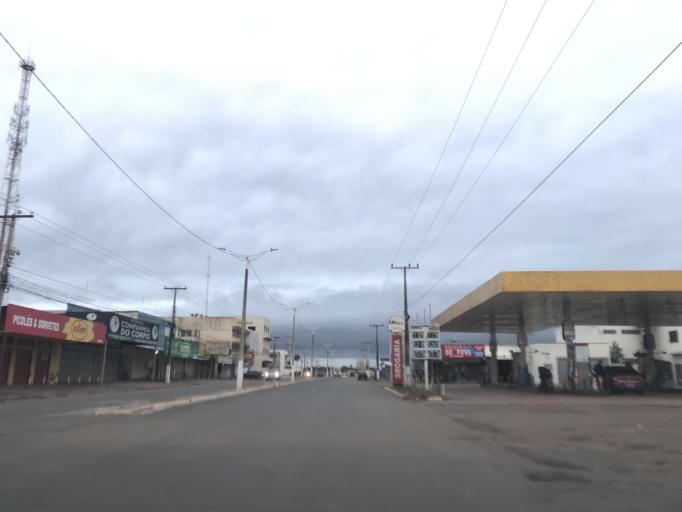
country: BR
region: Goias
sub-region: Luziania
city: Luziania
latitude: -16.2367
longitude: -47.9419
